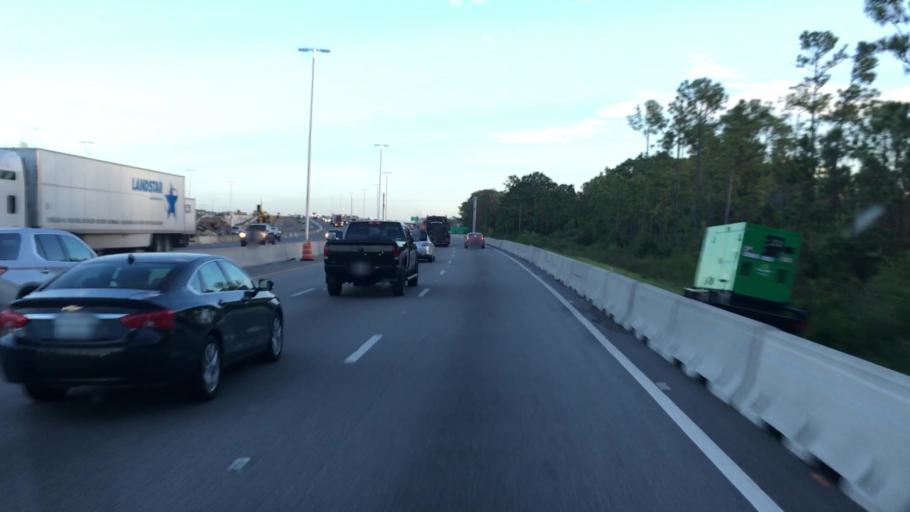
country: US
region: Florida
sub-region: Volusia County
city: Daytona Beach
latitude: 29.1779
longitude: -81.0888
